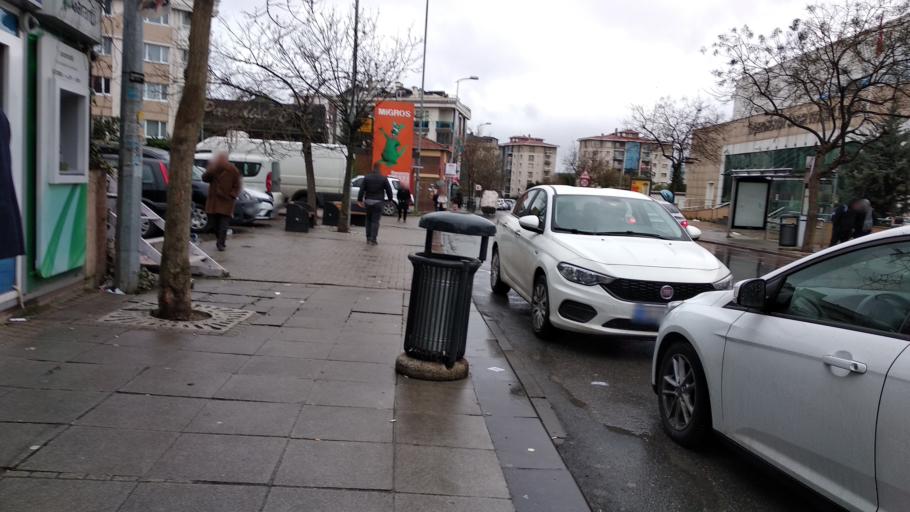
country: TR
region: Istanbul
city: Samandira
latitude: 41.0228
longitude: 29.1850
